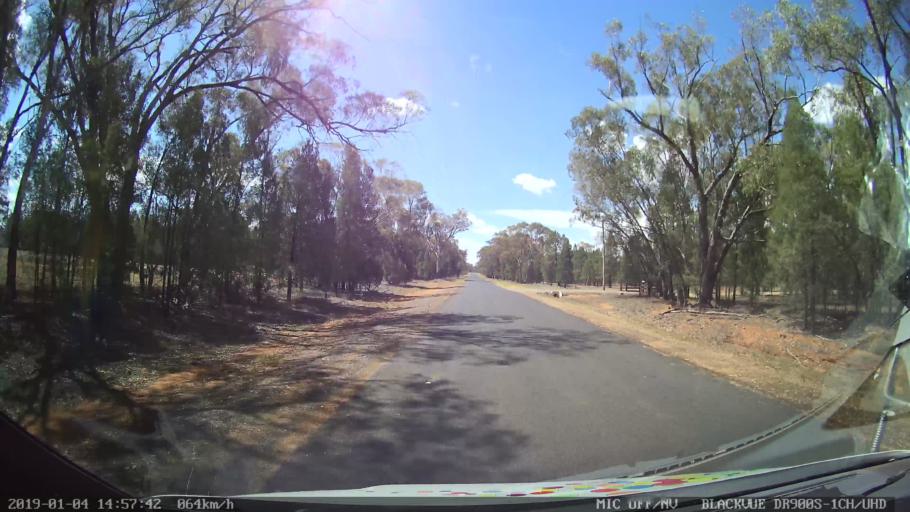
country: AU
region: New South Wales
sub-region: Gilgandra
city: Gilgandra
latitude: -31.9635
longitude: 148.6306
